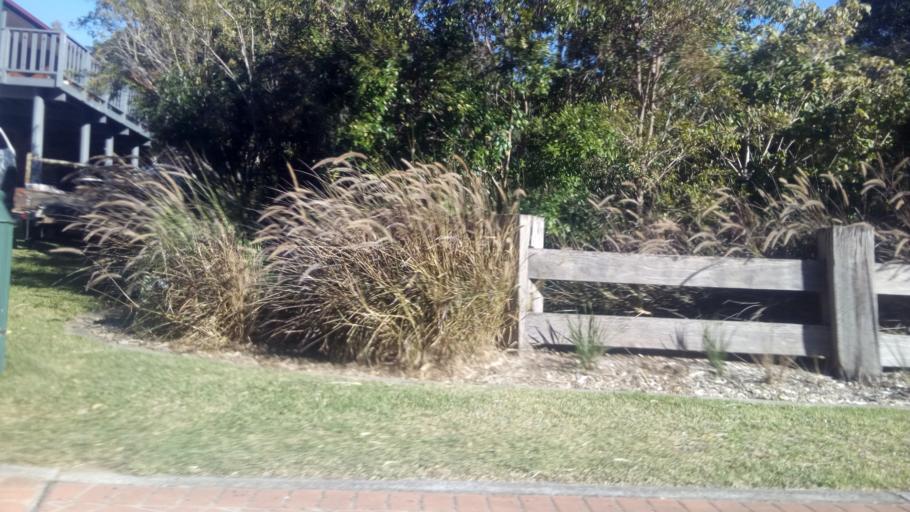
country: AU
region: New South Wales
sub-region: Wollongong
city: Mount Keira
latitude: -34.4152
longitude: 150.8471
